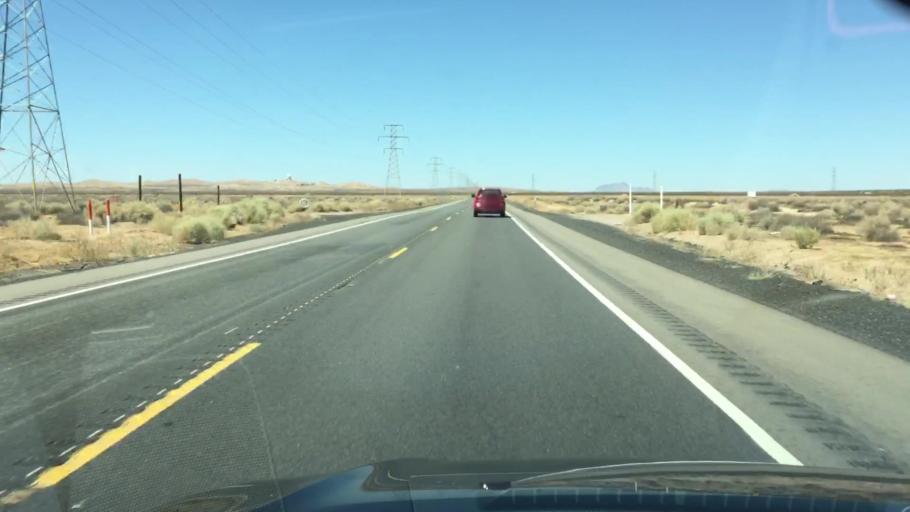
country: US
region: California
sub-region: Kern County
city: Boron
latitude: 35.0271
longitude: -117.5513
